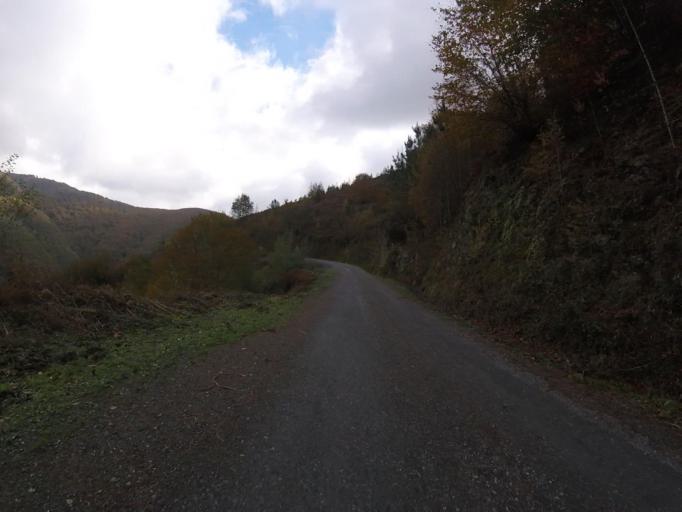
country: ES
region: Navarre
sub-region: Provincia de Navarra
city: Goizueta
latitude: 43.2247
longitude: -1.8256
